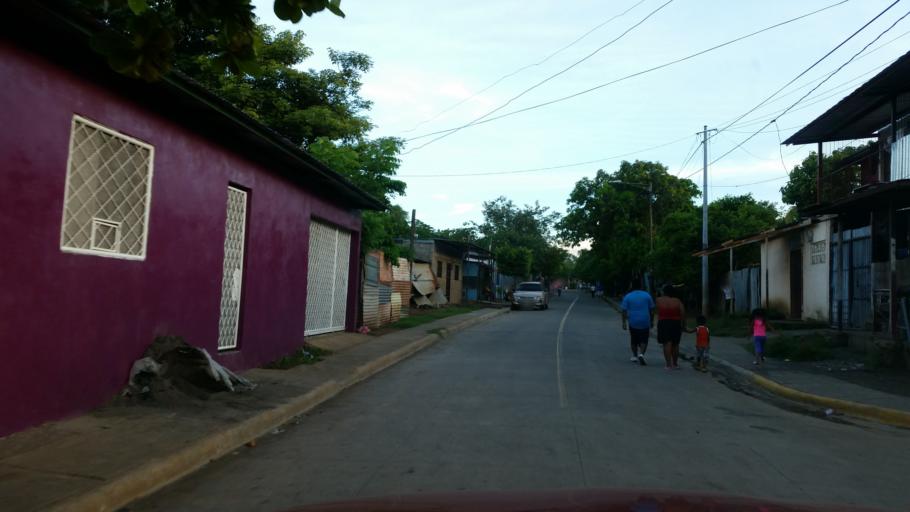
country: NI
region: Managua
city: Managua
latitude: 12.1318
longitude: -86.2866
